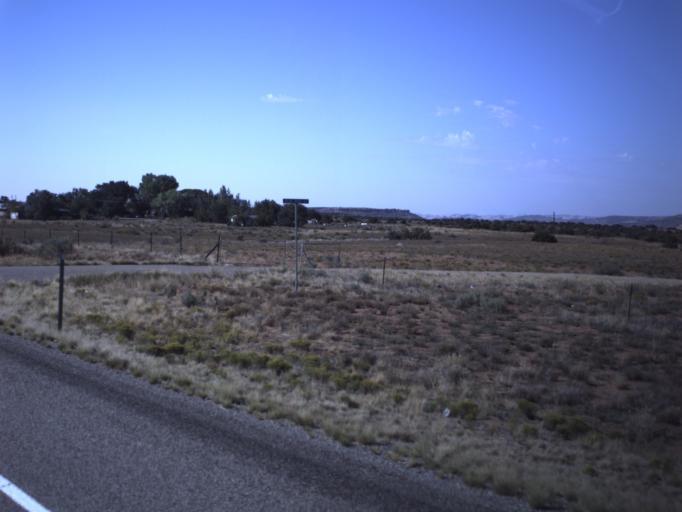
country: US
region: Utah
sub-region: San Juan County
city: Blanding
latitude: 37.4713
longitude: -109.4670
